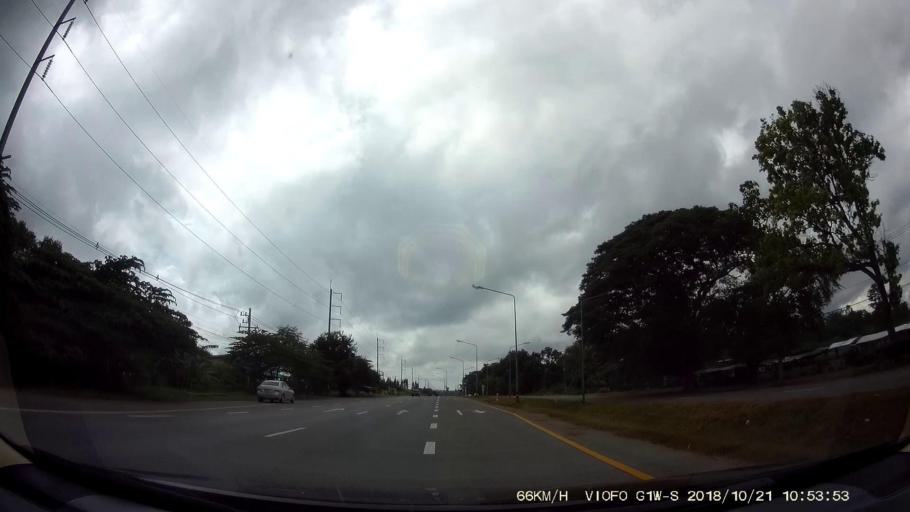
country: TH
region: Chaiyaphum
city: Khon Sawan
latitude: 15.9598
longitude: 102.1796
